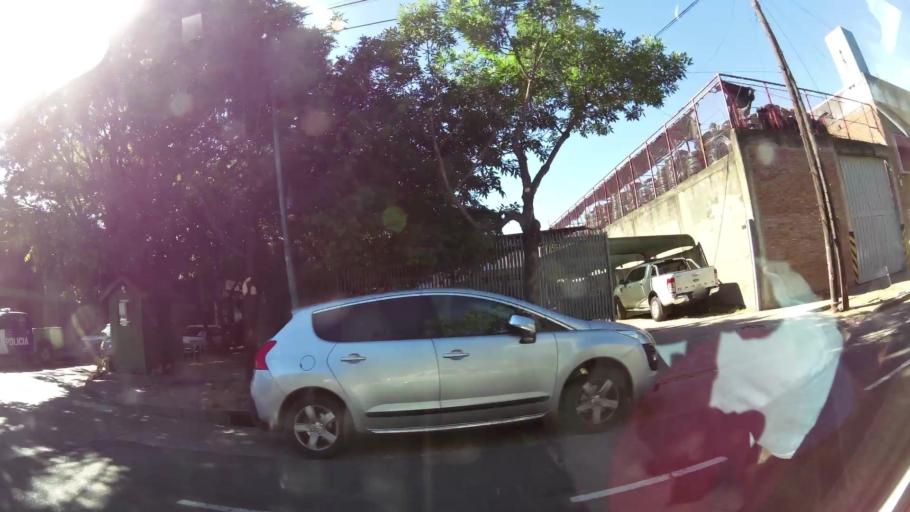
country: AR
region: Buenos Aires
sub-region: Partido de General San Martin
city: General San Martin
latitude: -34.5442
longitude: -58.5185
